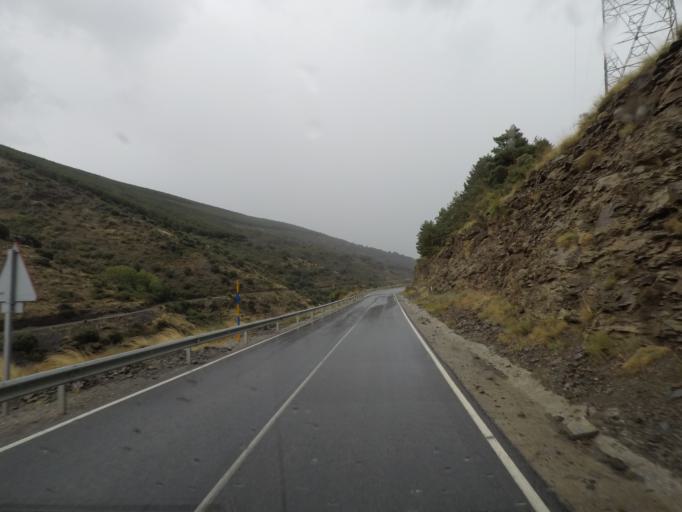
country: ES
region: Andalusia
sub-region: Provincia de Almeria
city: Bayarcal
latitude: 37.0730
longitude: -3.0193
